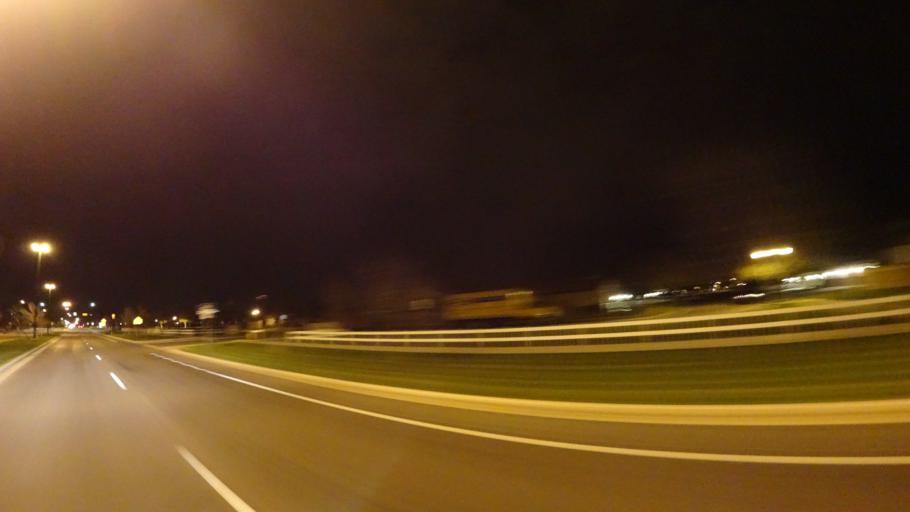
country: US
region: Arizona
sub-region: Maricopa County
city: Gilbert
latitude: 33.3523
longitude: -111.7045
